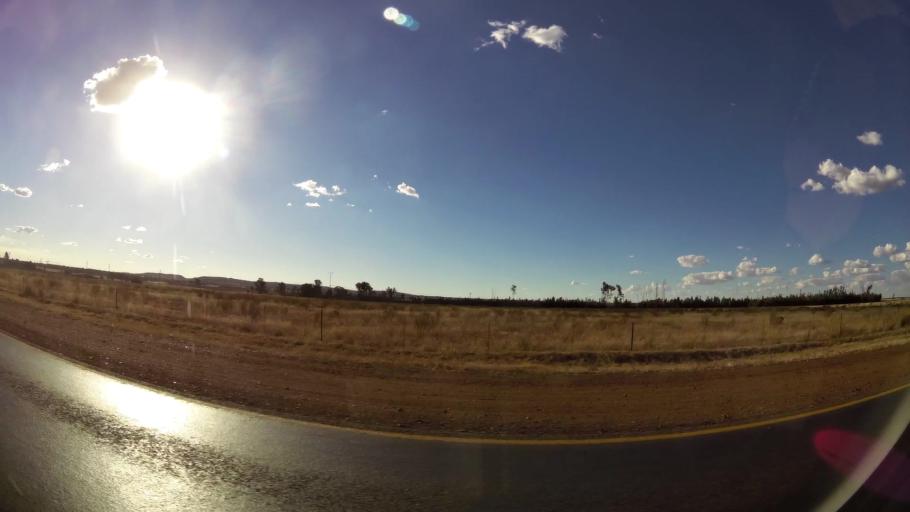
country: ZA
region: North-West
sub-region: Dr Kenneth Kaunda District Municipality
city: Klerksdorp
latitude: -26.8469
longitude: 26.7120
